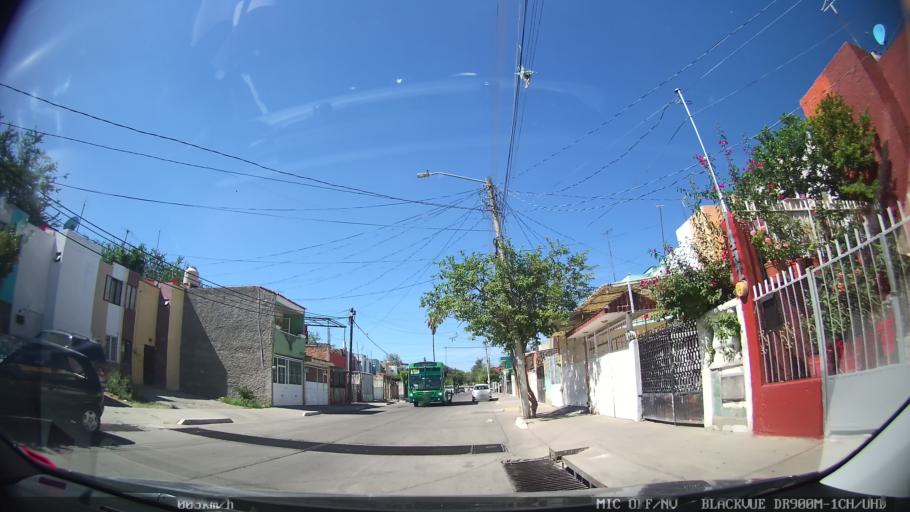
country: MX
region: Jalisco
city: Tlaquepaque
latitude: 20.6983
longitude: -103.2844
